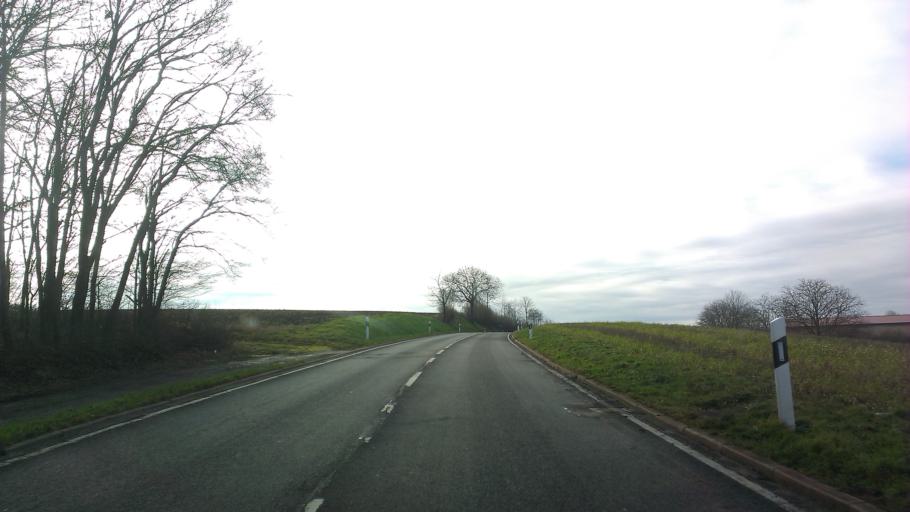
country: DE
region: Baden-Wuerttemberg
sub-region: Karlsruhe Region
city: Horrenberg
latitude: 49.2679
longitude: 8.7697
